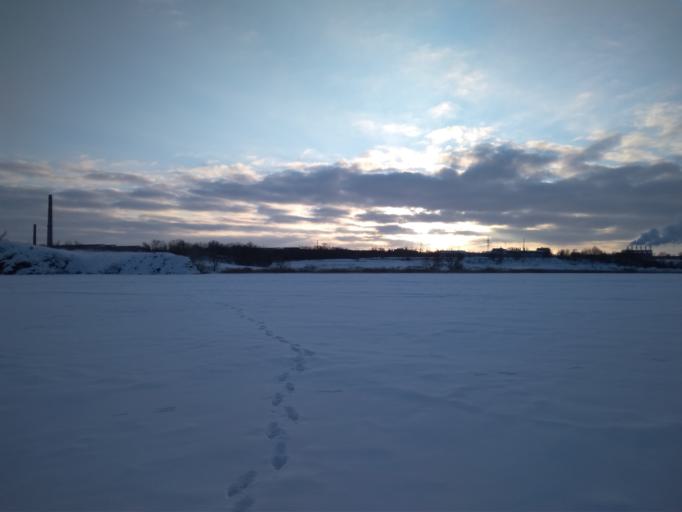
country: RU
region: Chelyabinsk
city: Troitsk
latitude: 54.0772
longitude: 61.5753
